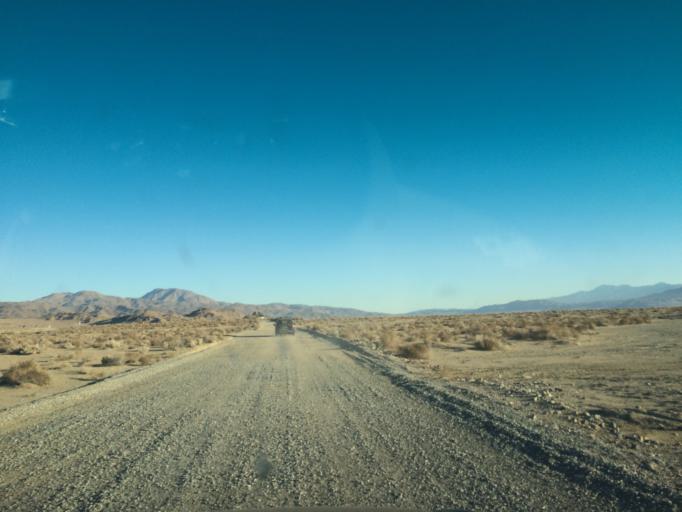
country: US
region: California
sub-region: San Bernardino County
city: Searles Valley
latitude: 35.6664
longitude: -117.3790
